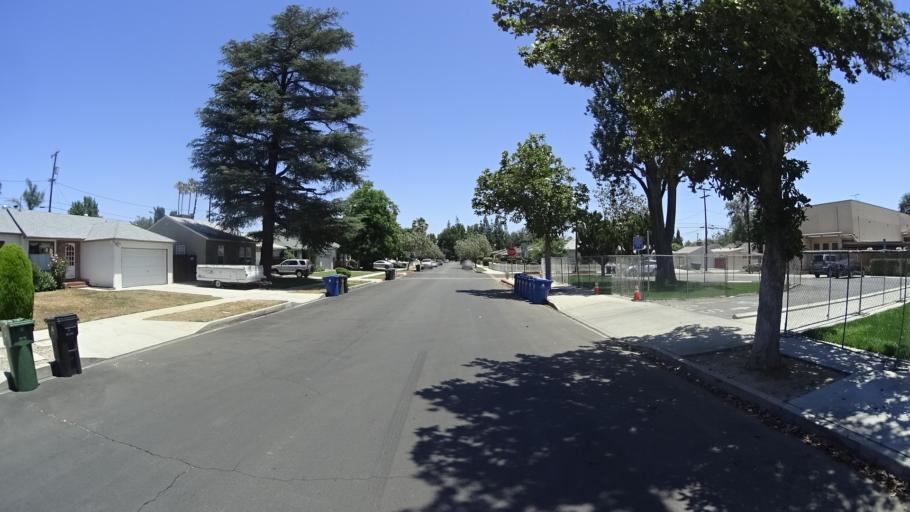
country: US
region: California
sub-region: Los Angeles County
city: Northridge
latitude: 34.1994
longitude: -118.5040
